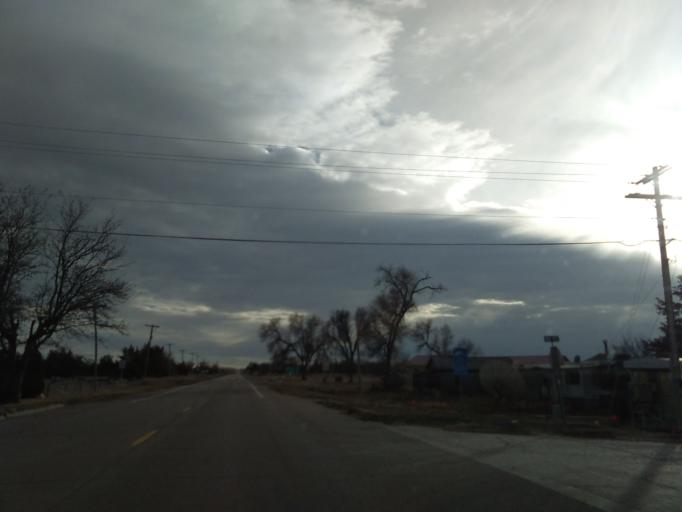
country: US
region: Nebraska
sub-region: Morrill County
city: Bridgeport
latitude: 41.6562
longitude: -103.0995
